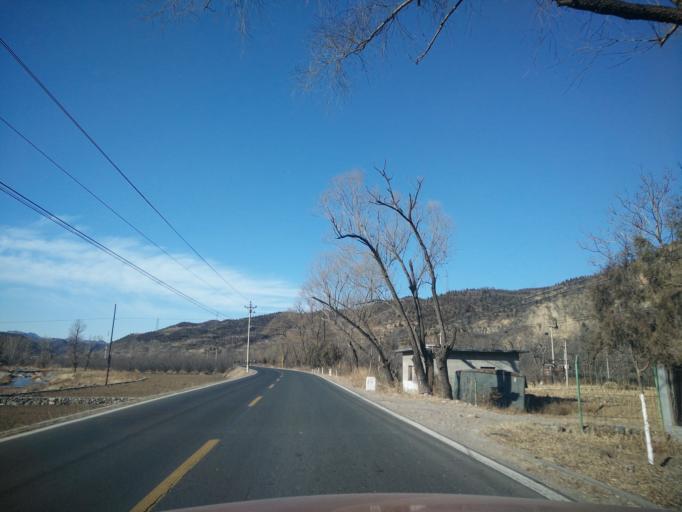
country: CN
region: Beijing
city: Zhaitang
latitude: 39.9924
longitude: 115.7569
